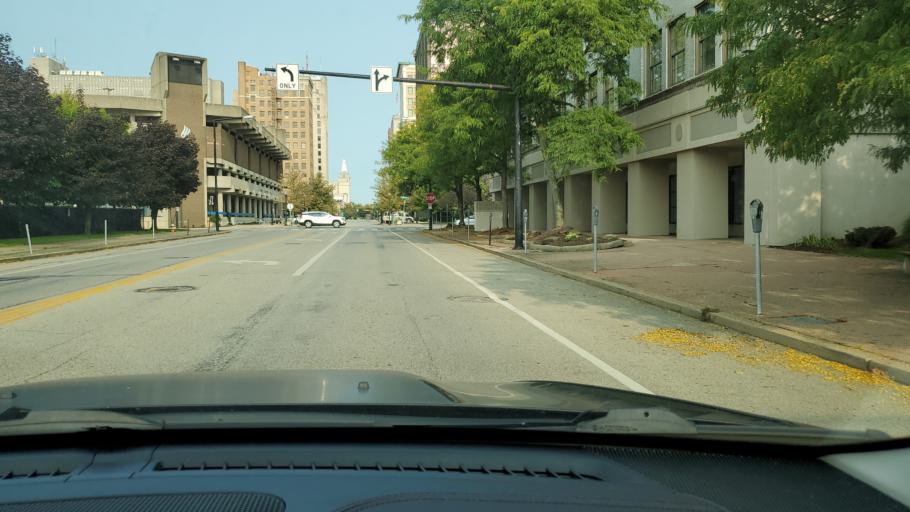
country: US
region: Ohio
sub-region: Mahoning County
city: Youngstown
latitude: 41.0987
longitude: -80.6462
